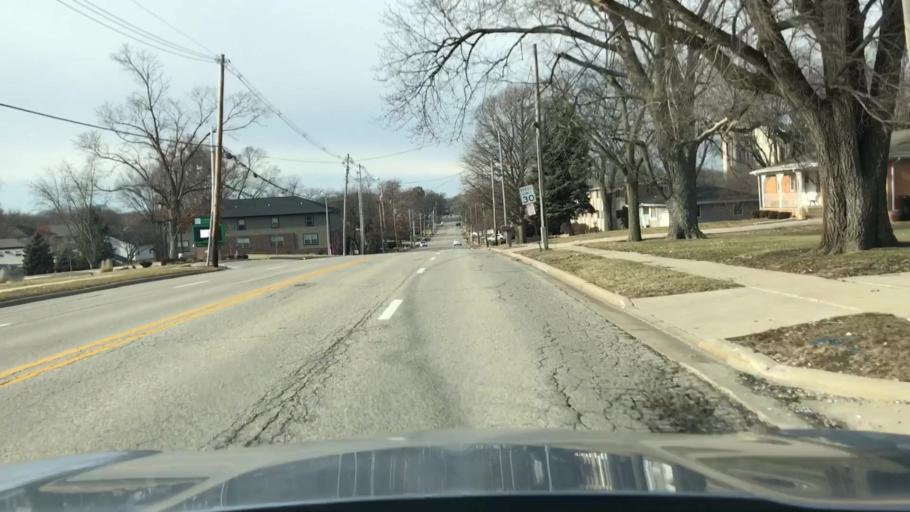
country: US
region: Illinois
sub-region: McLean County
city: Normal
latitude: 40.5051
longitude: -88.9757
